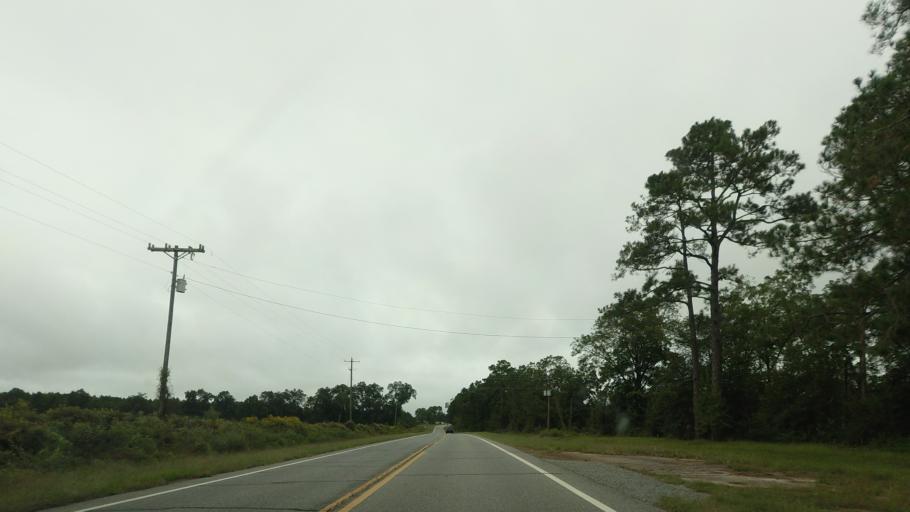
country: US
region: Georgia
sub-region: Irwin County
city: Ocilla
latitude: 31.5367
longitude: -83.2500
